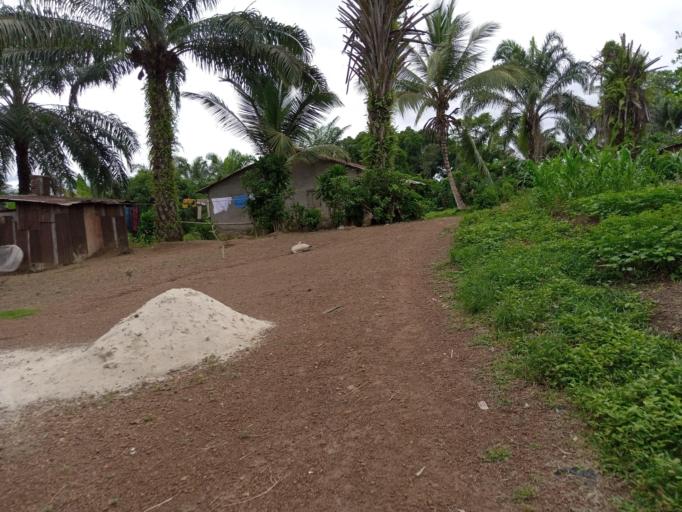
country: SL
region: Southern Province
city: Moyamba
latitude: 8.1694
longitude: -12.4271
